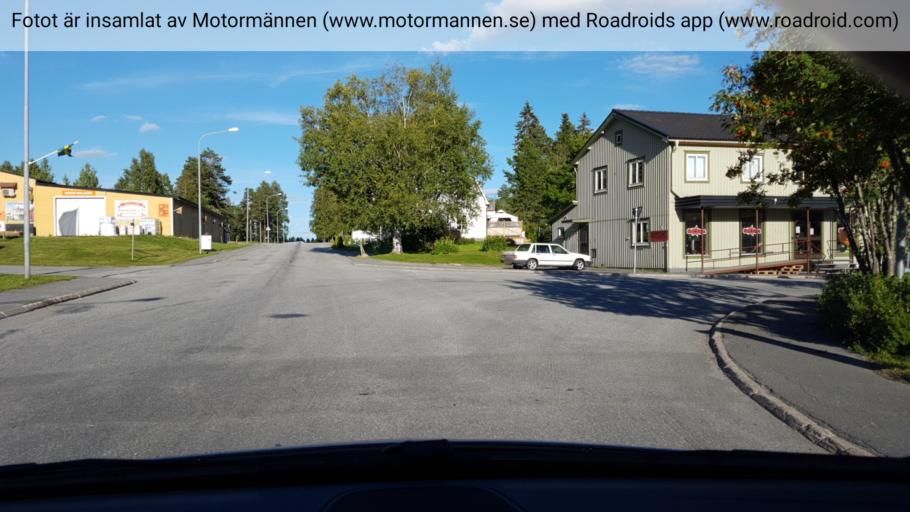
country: SE
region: Jaemtland
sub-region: Braecke Kommun
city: Braecke
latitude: 63.1674
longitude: 15.5977
